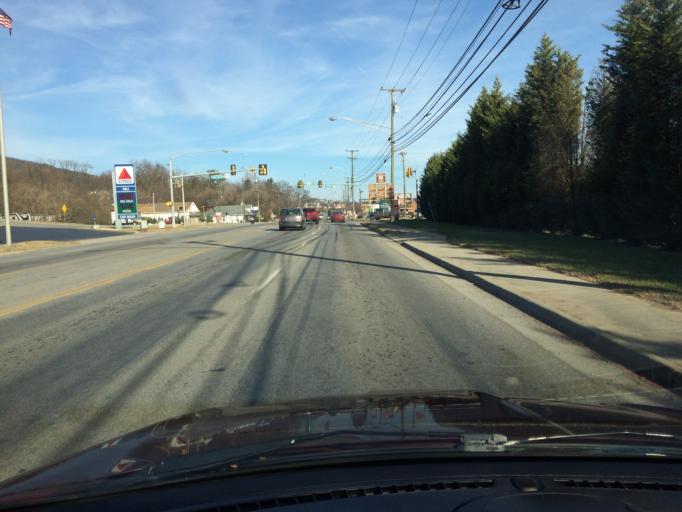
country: US
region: Virginia
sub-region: City of Salem
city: Salem
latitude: 37.2849
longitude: -80.1002
